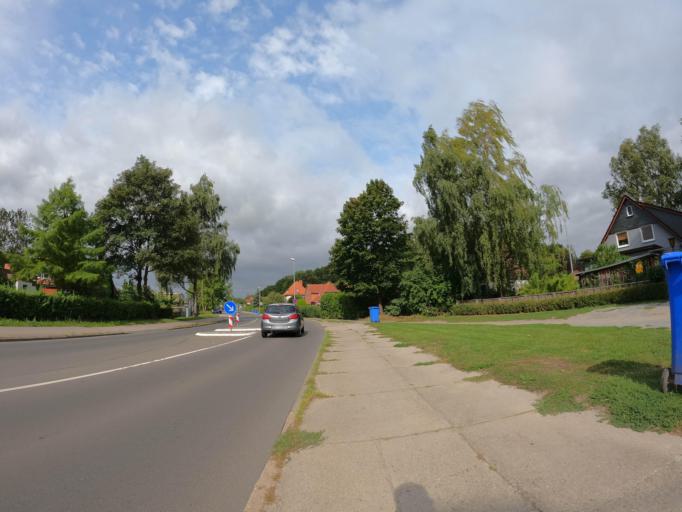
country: DE
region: Mecklenburg-Vorpommern
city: Stralsund
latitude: 54.3131
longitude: 13.0622
